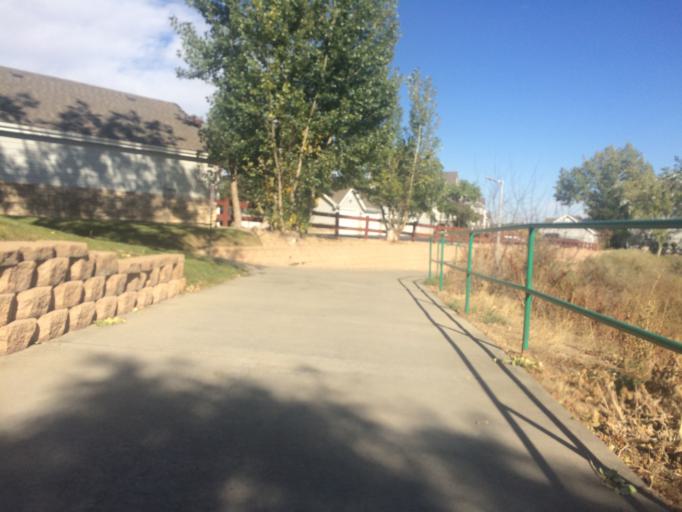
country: US
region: Colorado
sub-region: Broomfield County
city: Broomfield
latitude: 39.8789
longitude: -105.0788
